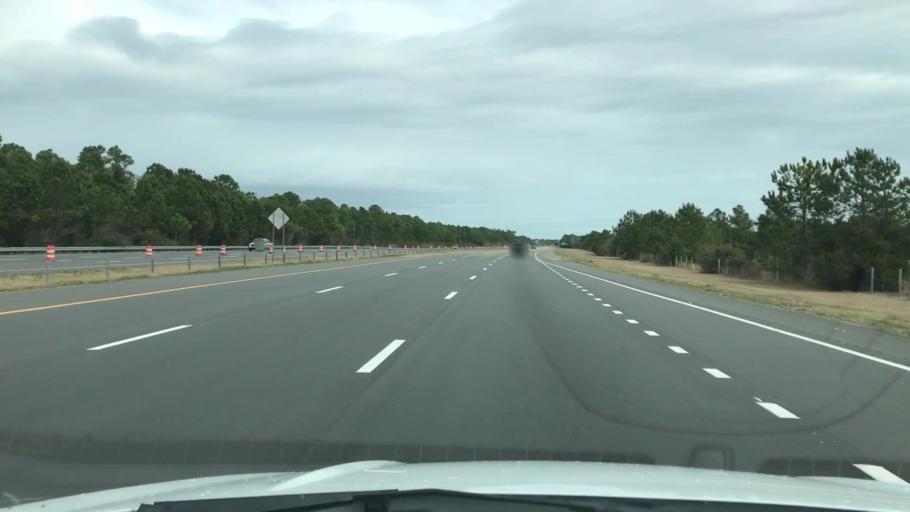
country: US
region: South Carolina
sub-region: Horry County
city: Socastee
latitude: 33.7111
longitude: -79.0074
